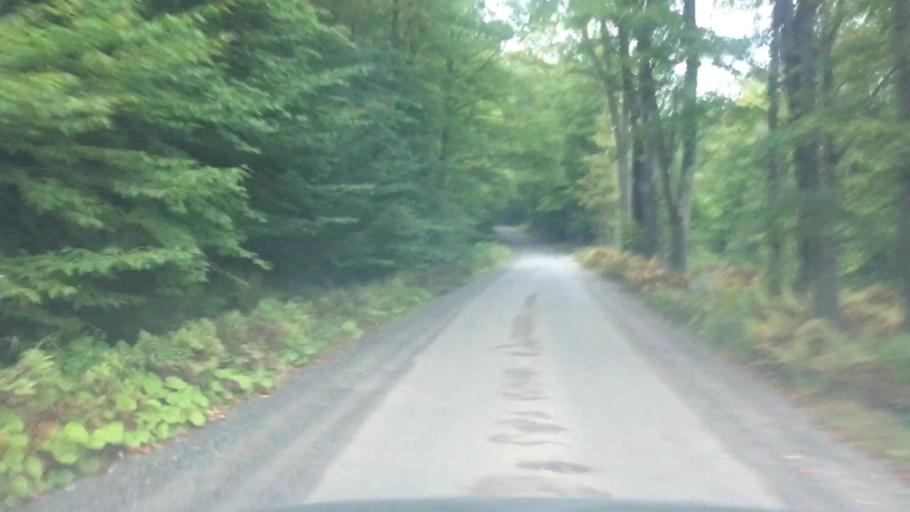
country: US
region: Vermont
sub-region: Windham County
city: Dover
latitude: 42.8449
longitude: -72.7690
